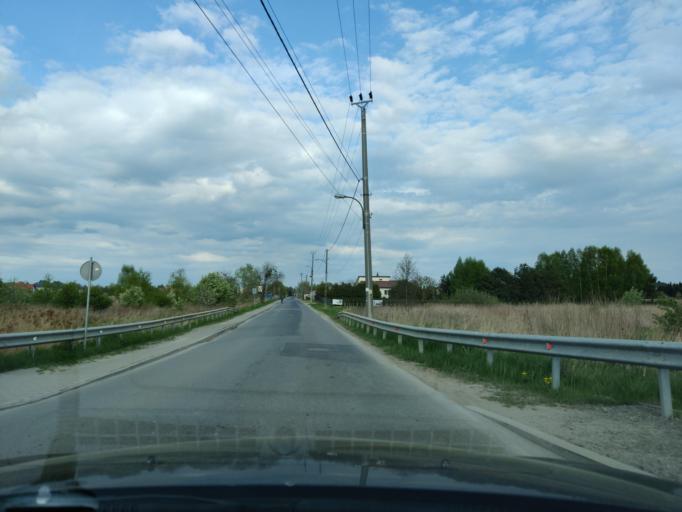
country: PL
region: Masovian Voivodeship
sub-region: Powiat piaseczynski
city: Konstancin-Jeziorna
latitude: 52.1306
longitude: 21.1207
